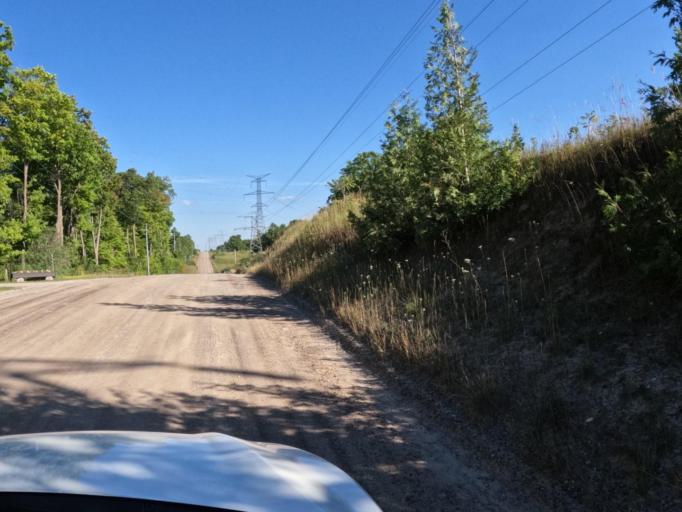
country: CA
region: Ontario
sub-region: Wellington County
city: Guelph
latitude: 43.4336
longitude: -80.1342
